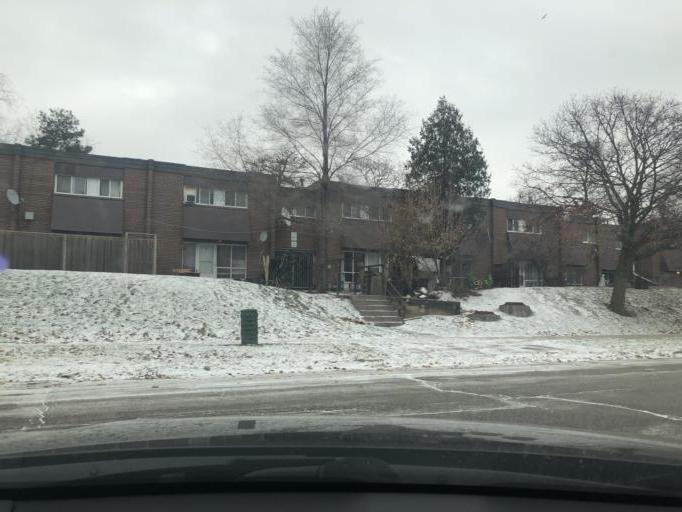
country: CA
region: Ontario
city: Scarborough
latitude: 43.7830
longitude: -79.3039
